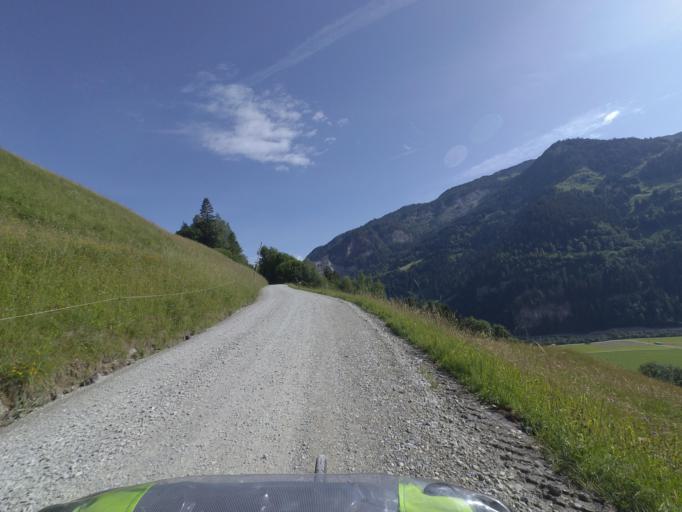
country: AT
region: Salzburg
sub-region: Politischer Bezirk Sankt Johann im Pongau
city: Dorfgastein
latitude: 47.2594
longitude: 13.0771
